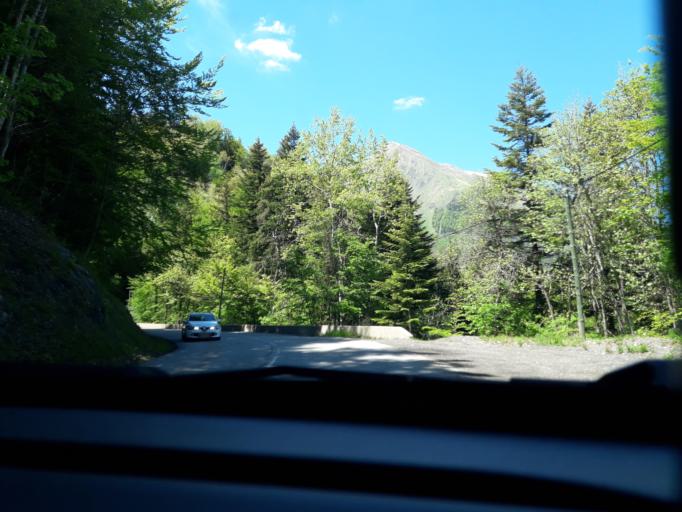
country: FR
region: Rhone-Alpes
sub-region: Departement de la Savoie
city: Saint-Martin-de-Belleville
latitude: 45.4191
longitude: 6.4869
